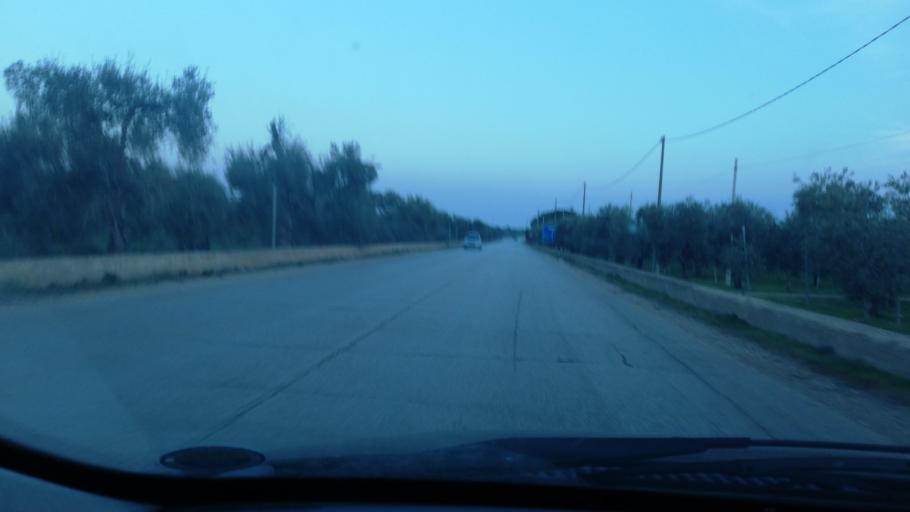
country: IT
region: Apulia
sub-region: Provincia di Bari
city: Bitonto
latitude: 41.1304
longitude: 16.7084
